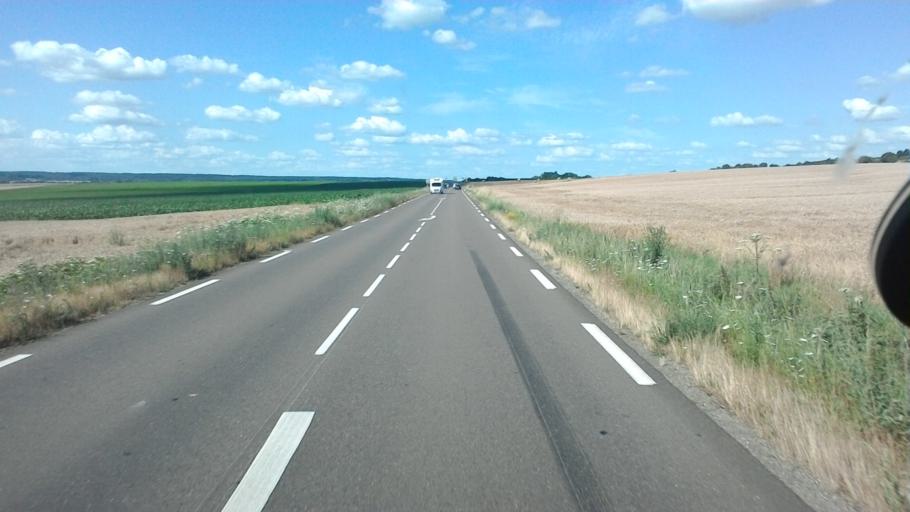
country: FR
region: Franche-Comte
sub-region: Departement de la Haute-Saone
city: Gy
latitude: 47.3942
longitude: 5.7920
